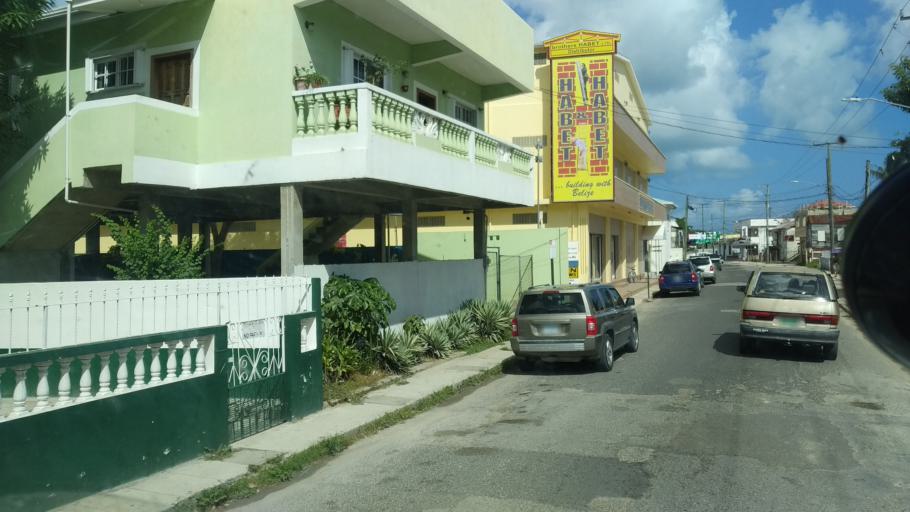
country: BZ
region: Belize
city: Belize City
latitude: 17.4949
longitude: -88.1960
